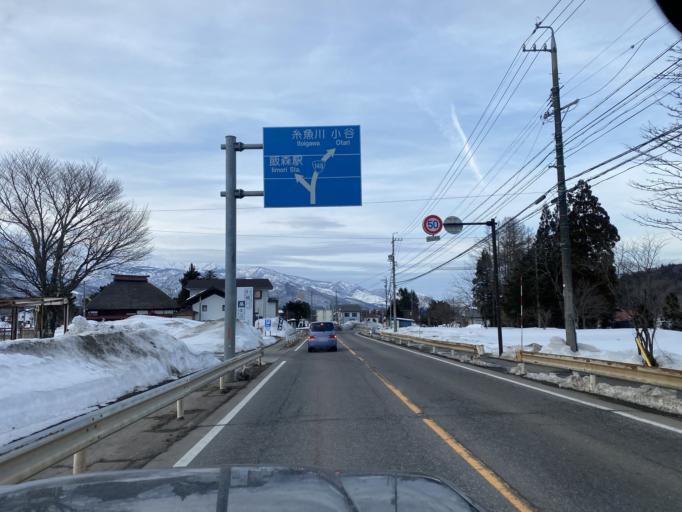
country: JP
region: Nagano
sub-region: Kitaazumi Gun
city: Hakuba
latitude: 36.6657
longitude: 137.8490
